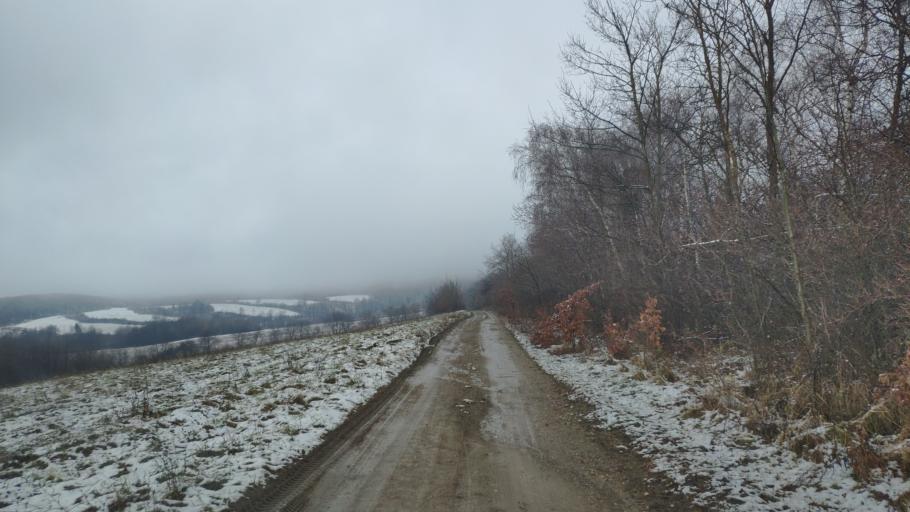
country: SK
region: Kosicky
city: Moldava nad Bodvou
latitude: 48.7361
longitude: 21.0916
